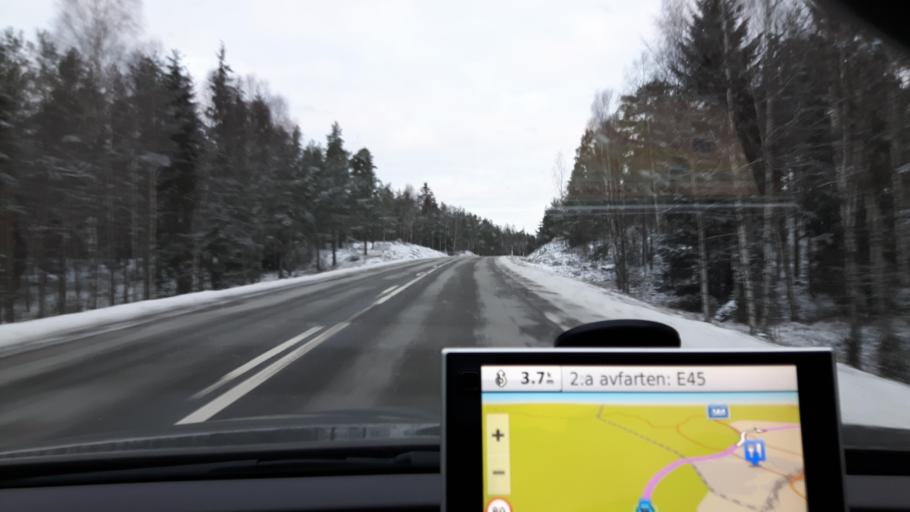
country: SE
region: Vaestra Goetaland
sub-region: Amals Kommun
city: Amal
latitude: 59.0237
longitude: 12.6795
